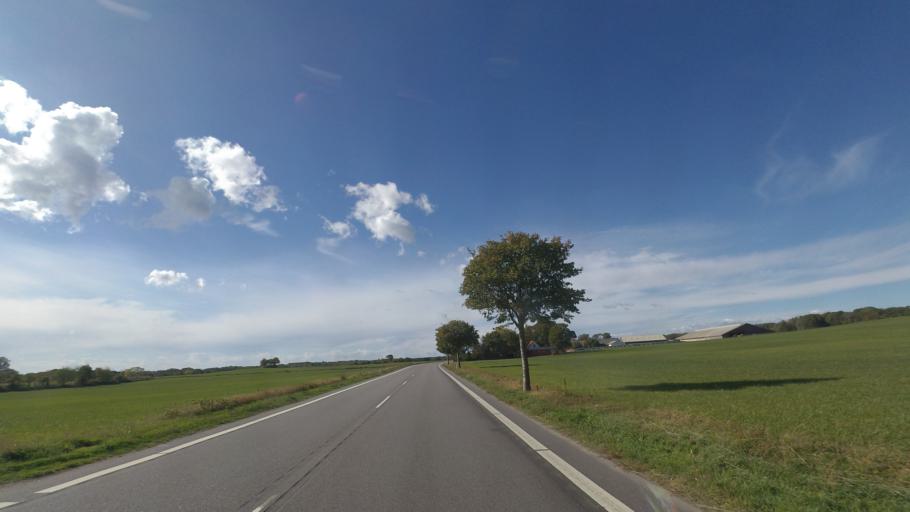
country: DK
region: Capital Region
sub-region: Bornholm Kommune
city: Ronne
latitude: 55.0746
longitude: 14.7843
